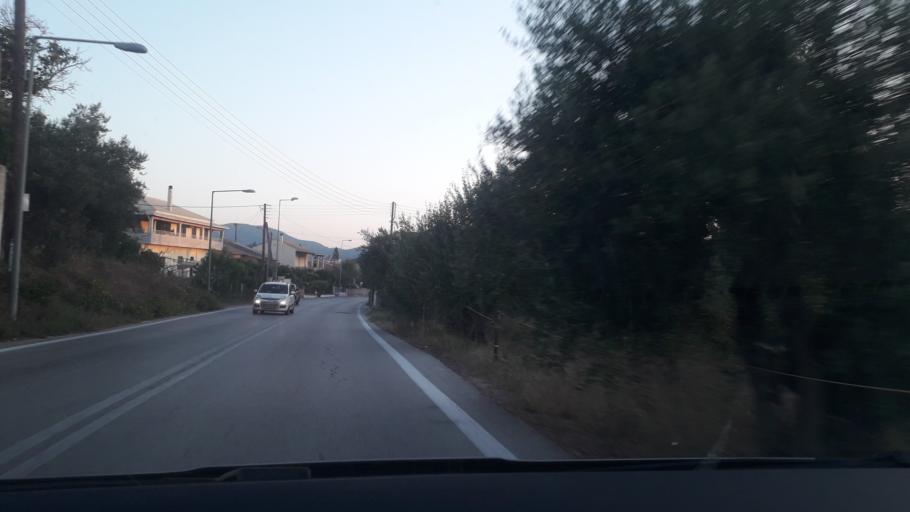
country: GR
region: Ionian Islands
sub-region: Nomos Kerkyras
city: Agios Matthaios
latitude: 39.4651
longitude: 19.9128
